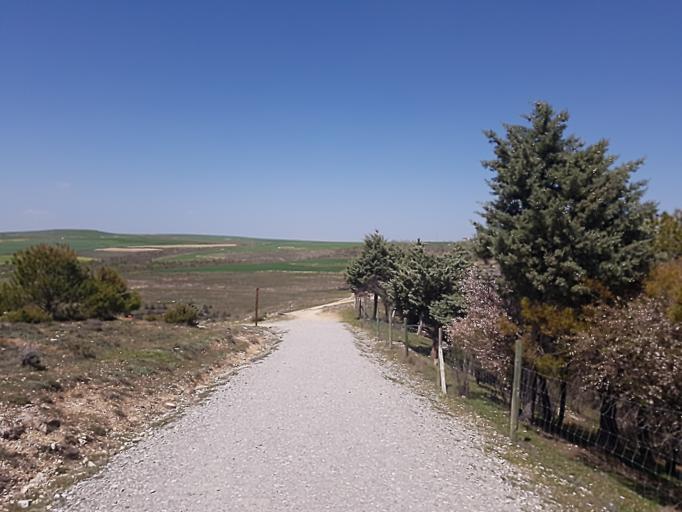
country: ES
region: Castille and Leon
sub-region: Provincia de Segovia
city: Segovia
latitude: 40.9517
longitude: -4.1345
